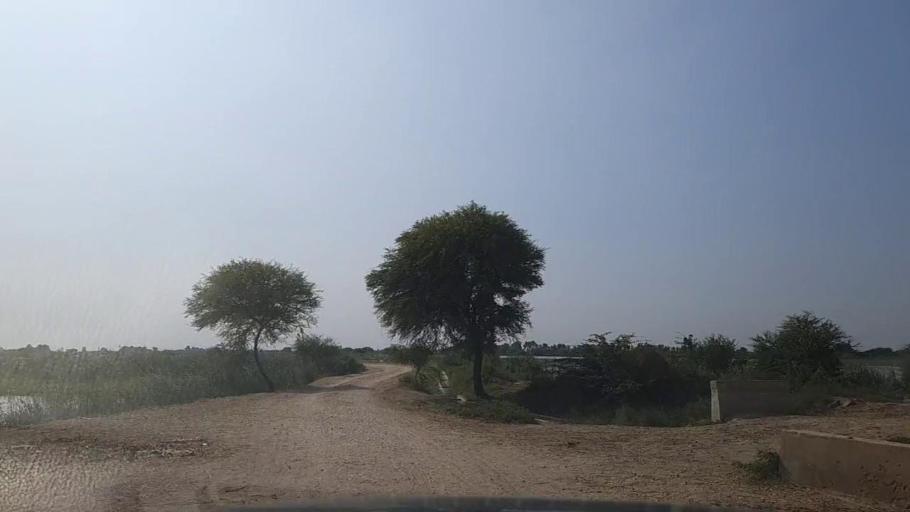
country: PK
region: Sindh
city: Chuhar Jamali
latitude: 24.5495
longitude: 67.9186
